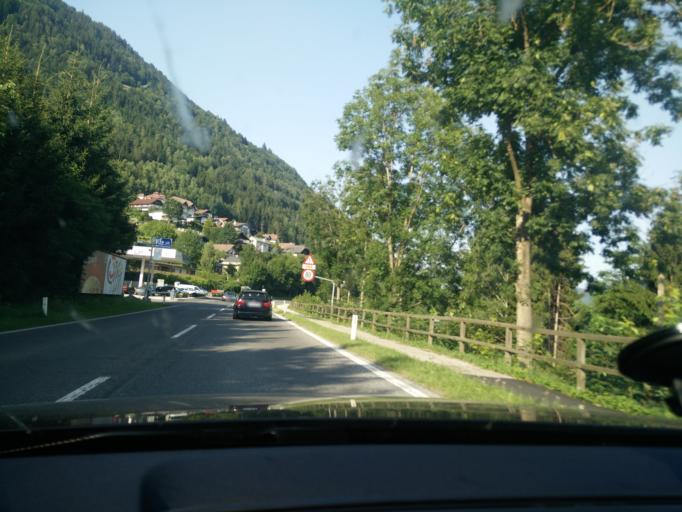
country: AT
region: Carinthia
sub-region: Politischer Bezirk Villach Land
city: Wernberg
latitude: 46.6653
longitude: 13.9257
